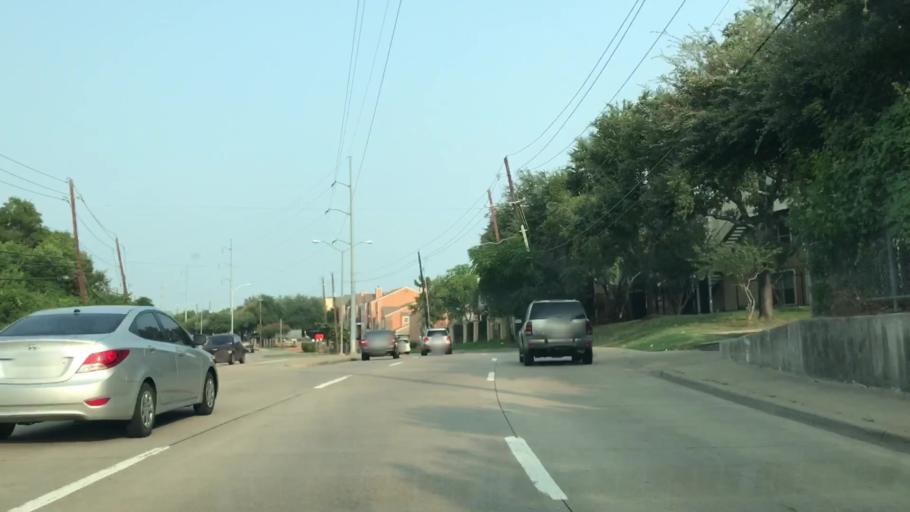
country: US
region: Texas
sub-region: Dallas County
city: Richardson
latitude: 32.9093
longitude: -96.7156
